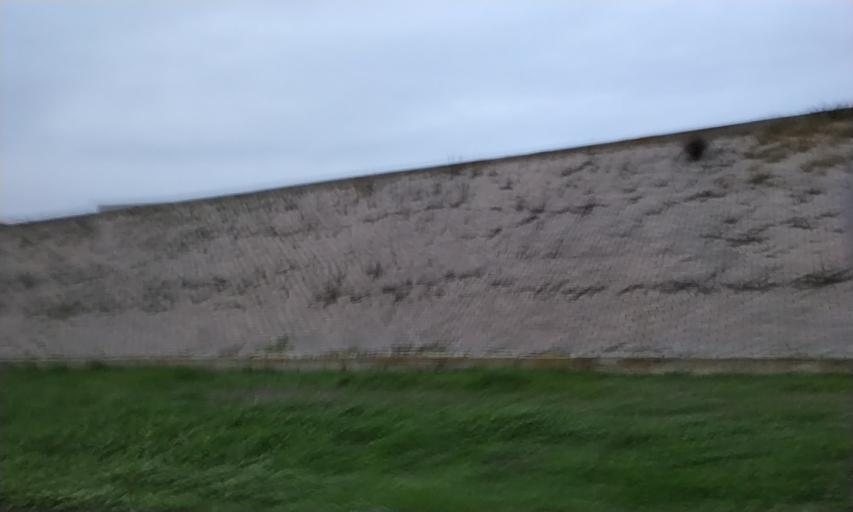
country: PT
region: Setubal
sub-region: Setubal
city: Setubal
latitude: 38.4980
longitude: -8.8374
